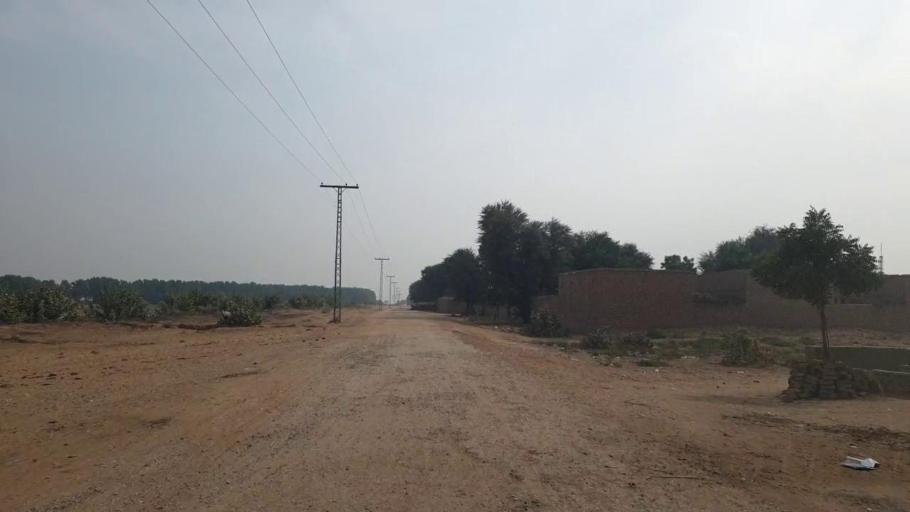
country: PK
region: Sindh
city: Sann
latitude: 26.0320
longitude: 68.1358
